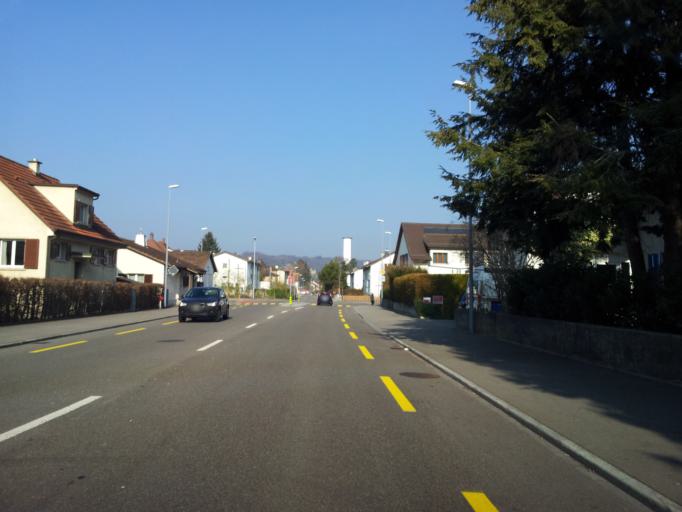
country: CH
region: Aargau
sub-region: Bezirk Baden
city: Wettingen
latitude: 47.4656
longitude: 8.3216
